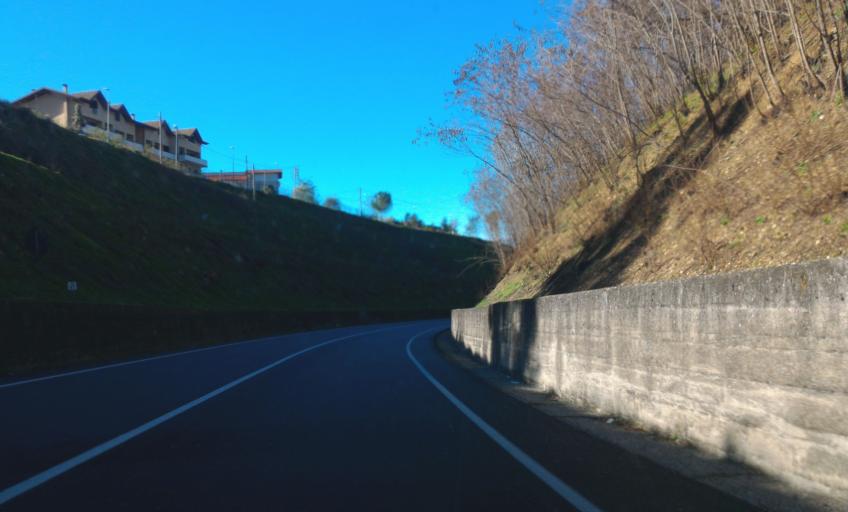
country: IT
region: Calabria
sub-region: Provincia di Cosenza
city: Rovito
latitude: 39.2966
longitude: 16.3066
